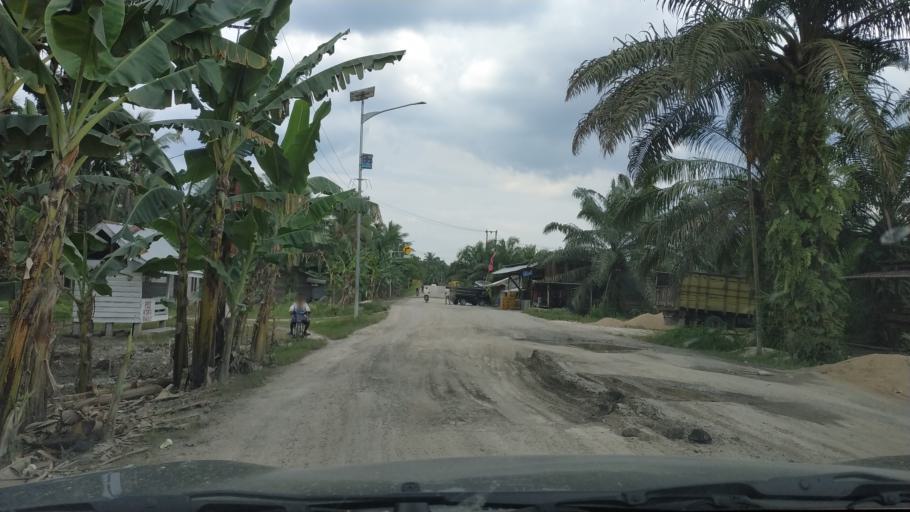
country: ID
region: Riau
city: Sungaisalak
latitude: -0.5641
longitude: 102.9636
